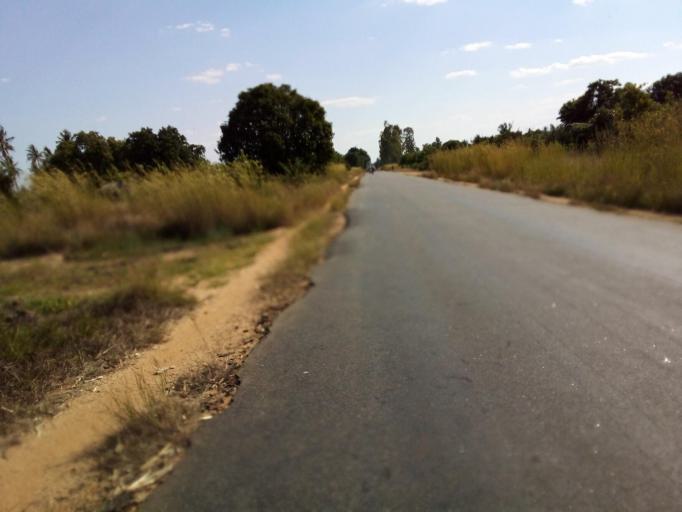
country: MZ
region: Zambezia
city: Quelimane
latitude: -17.5760
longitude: 36.6382
